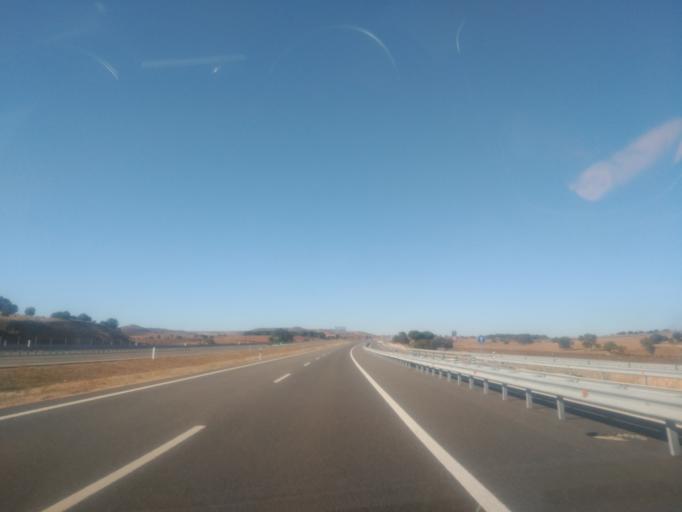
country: ES
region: Castille and Leon
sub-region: Provincia de Burgos
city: Fuentespina
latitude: 41.6371
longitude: -3.7066
